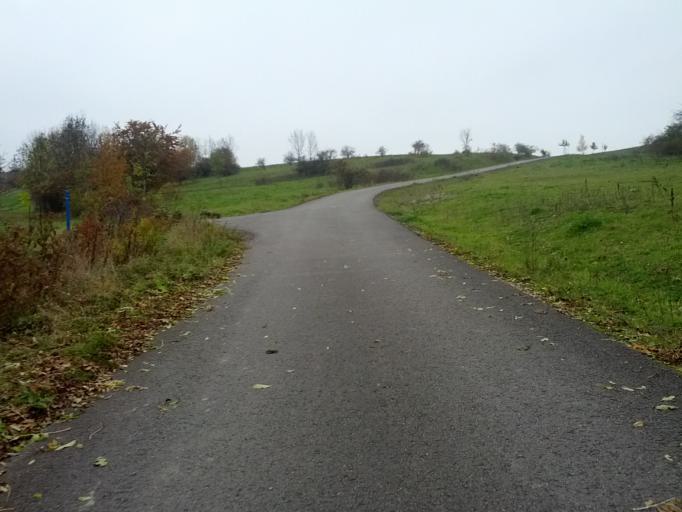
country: DE
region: Thuringia
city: Thal
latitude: 50.9652
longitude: 10.3787
